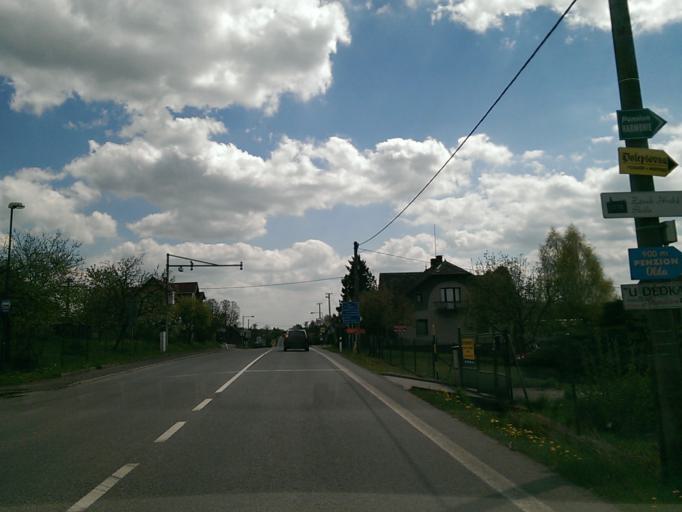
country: CZ
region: Liberecky
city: Rovensko pod Troskami
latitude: 50.5508
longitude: 15.2141
